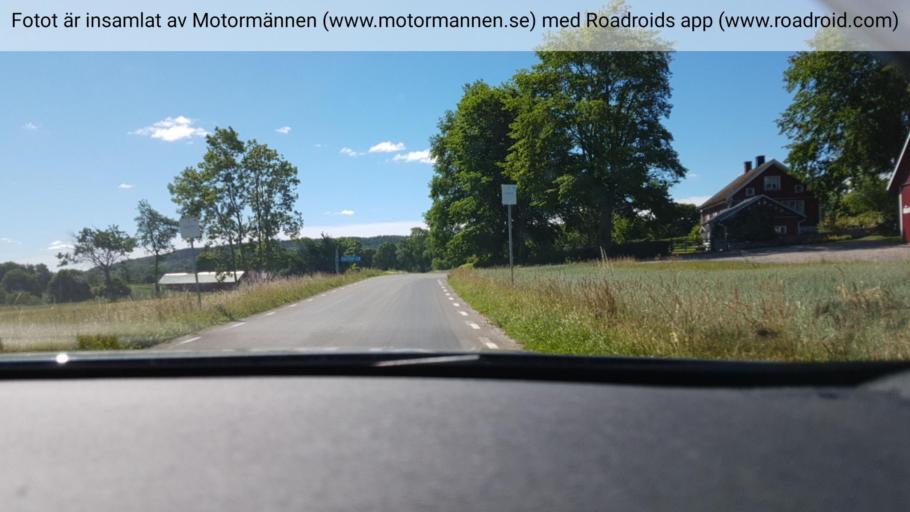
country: SE
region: Vaestra Goetaland
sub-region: Skovde Kommun
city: Skultorp
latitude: 58.2397
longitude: 13.7889
